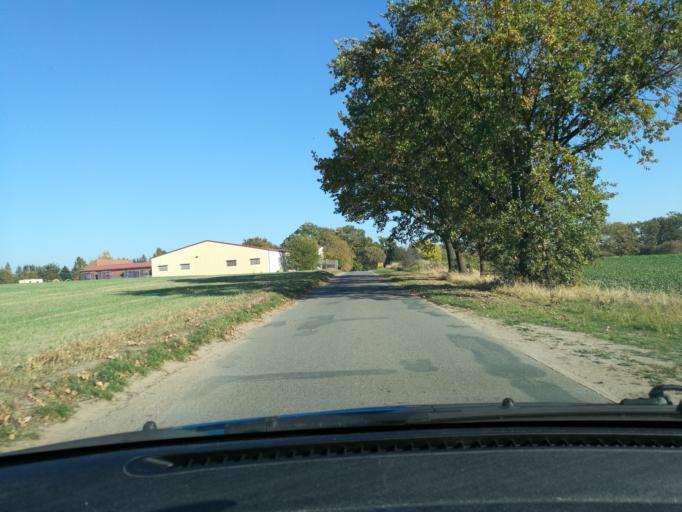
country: DE
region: Lower Saxony
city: Vastorf
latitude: 53.2044
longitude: 10.5417
